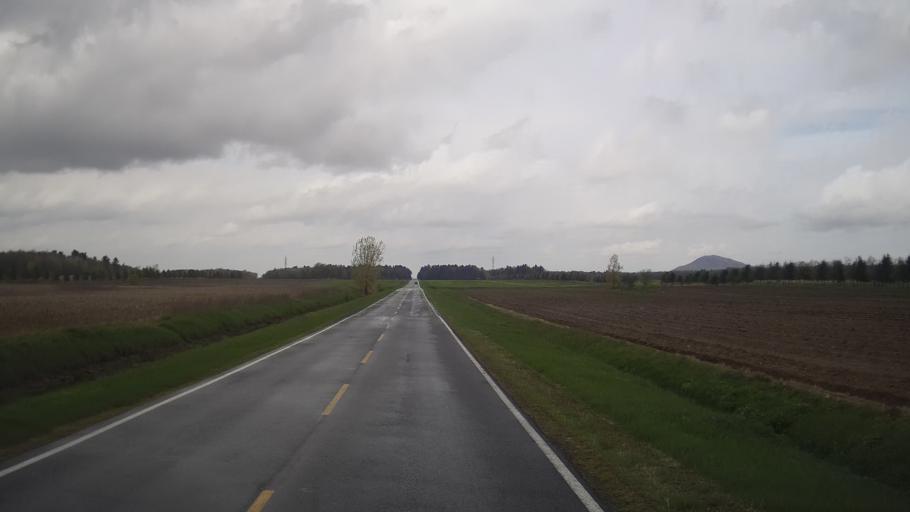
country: CA
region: Quebec
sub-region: Monteregie
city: Farnham
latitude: 45.3053
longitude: -73.1143
